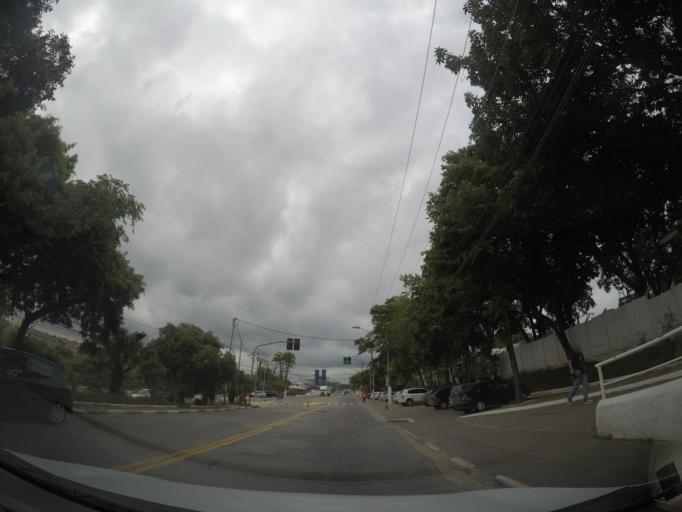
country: BR
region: Sao Paulo
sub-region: Aruja
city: Aruja
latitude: -23.4145
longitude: -46.4084
